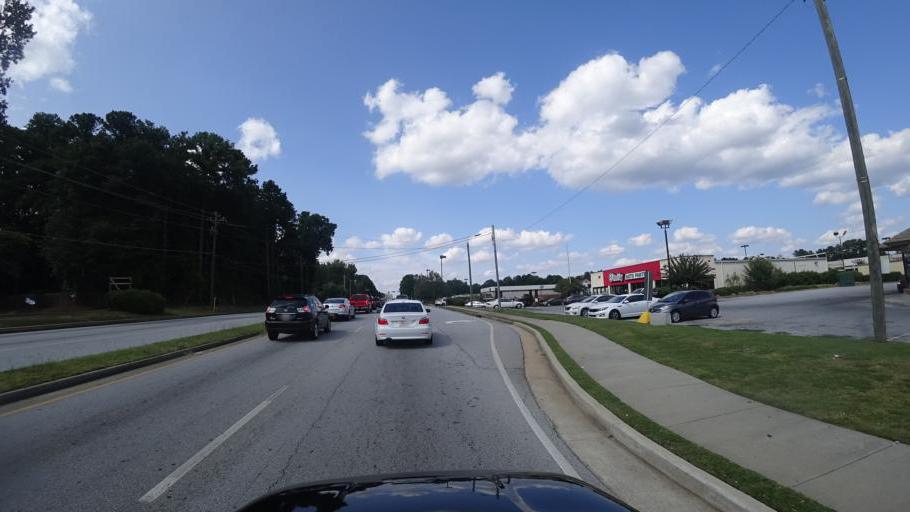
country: US
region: Georgia
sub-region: DeKalb County
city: Stone Mountain
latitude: 33.8039
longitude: -84.1936
